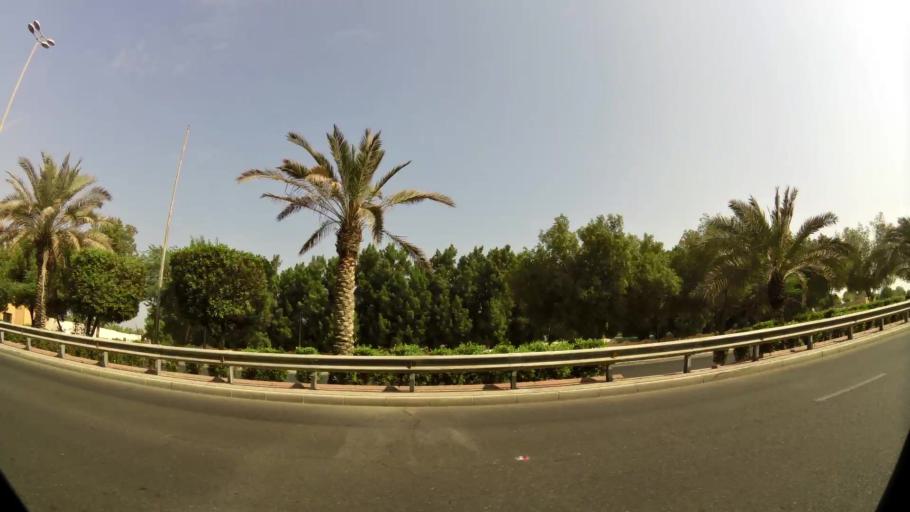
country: KW
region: Al Ahmadi
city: Al Fintas
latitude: 29.1836
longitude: 48.1180
